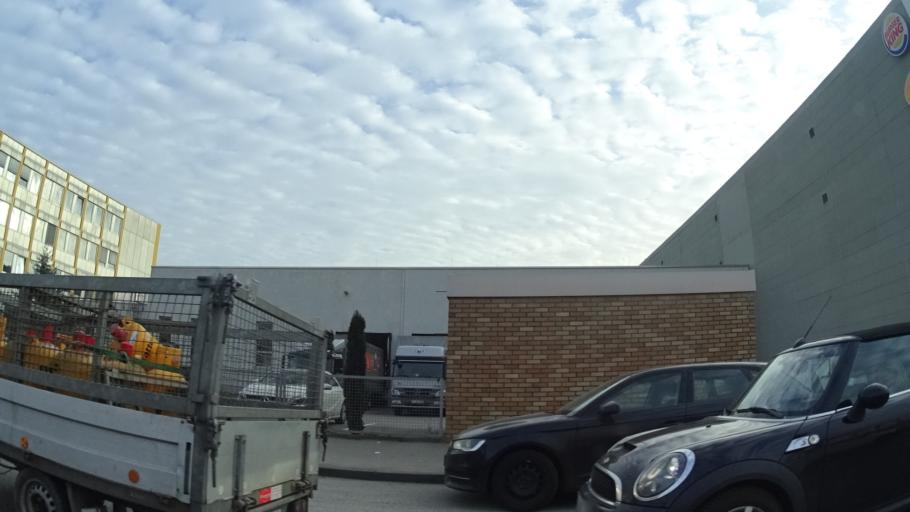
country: DE
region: Baden-Wuerttemberg
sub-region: Regierungsbezirk Stuttgart
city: Leinfelden-Echterdingen
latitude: 48.7232
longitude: 9.1267
